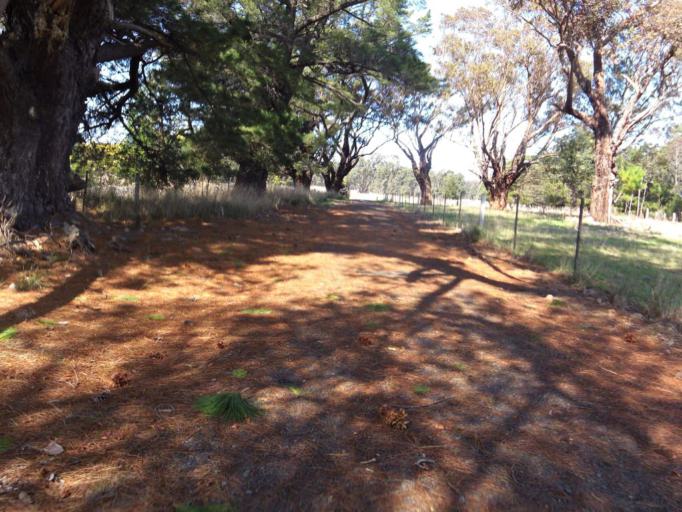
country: AU
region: Victoria
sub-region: Murrindindi
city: Alexandra
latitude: -36.9806
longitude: 145.7179
